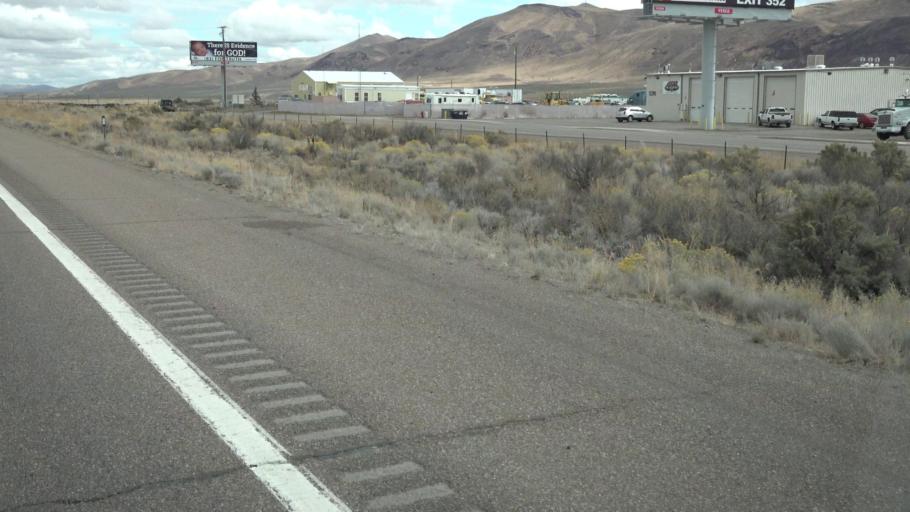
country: US
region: Nevada
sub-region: Elko County
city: Elko
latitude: 40.8753
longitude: -115.7222
